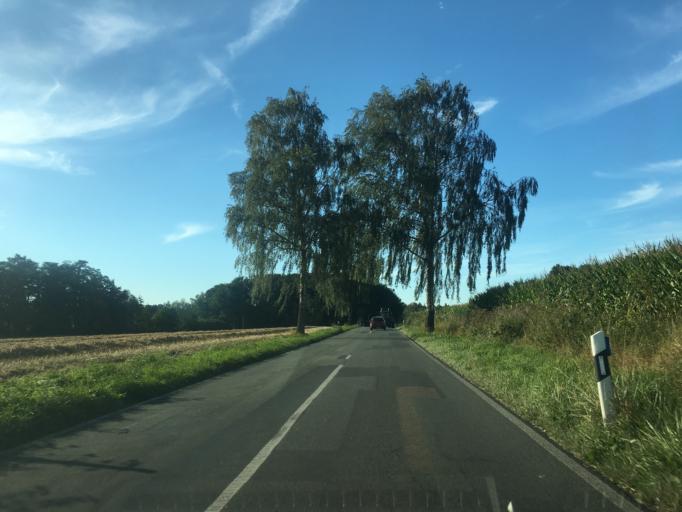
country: DE
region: North Rhine-Westphalia
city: Olfen
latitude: 51.7260
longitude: 7.3453
